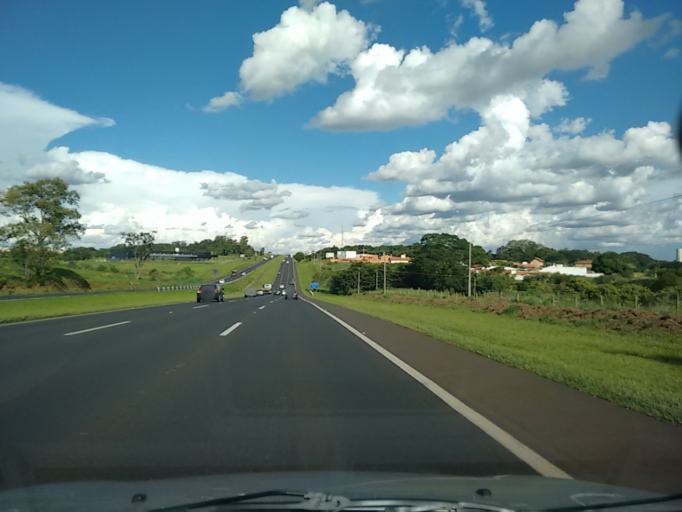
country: BR
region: Sao Paulo
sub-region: Ibate
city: Ibate
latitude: -21.9720
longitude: -47.9472
